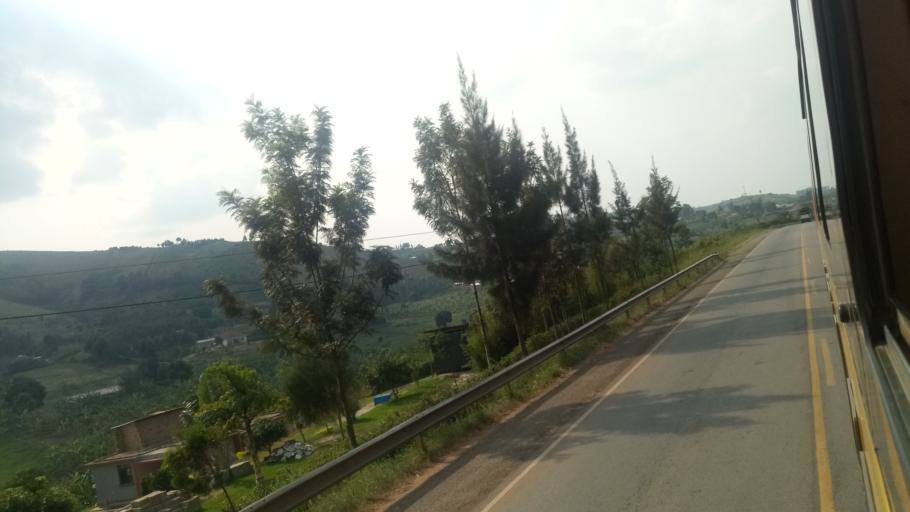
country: UG
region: Western Region
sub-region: Mbarara District
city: Mbarara
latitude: -0.5382
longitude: 30.7149
